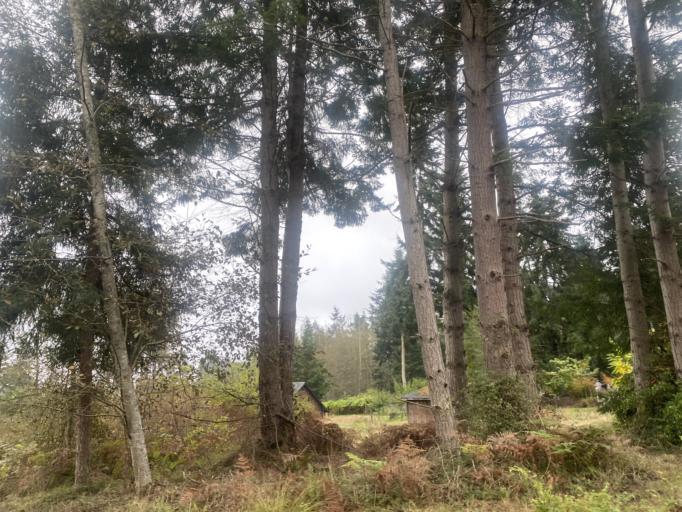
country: US
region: Washington
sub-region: Island County
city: Freeland
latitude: 48.0859
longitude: -122.5644
